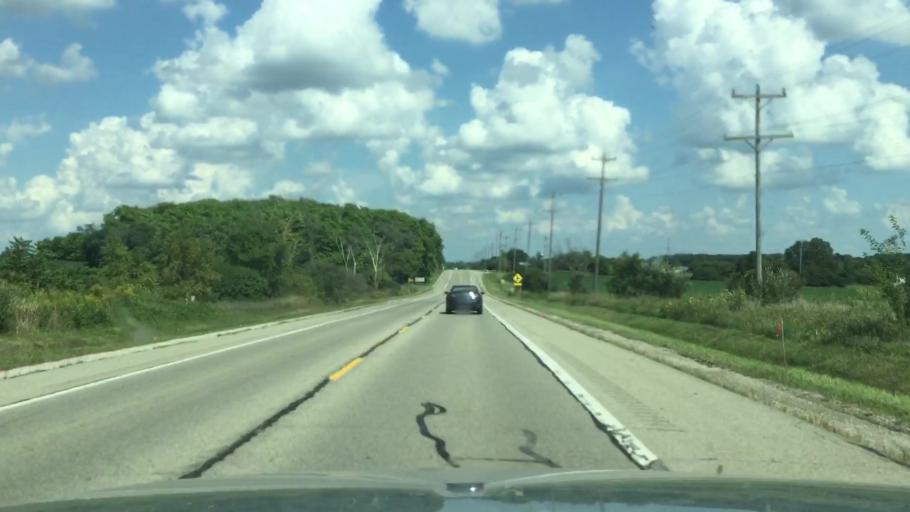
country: US
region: Michigan
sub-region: Washtenaw County
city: Saline
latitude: 42.1549
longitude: -83.8099
